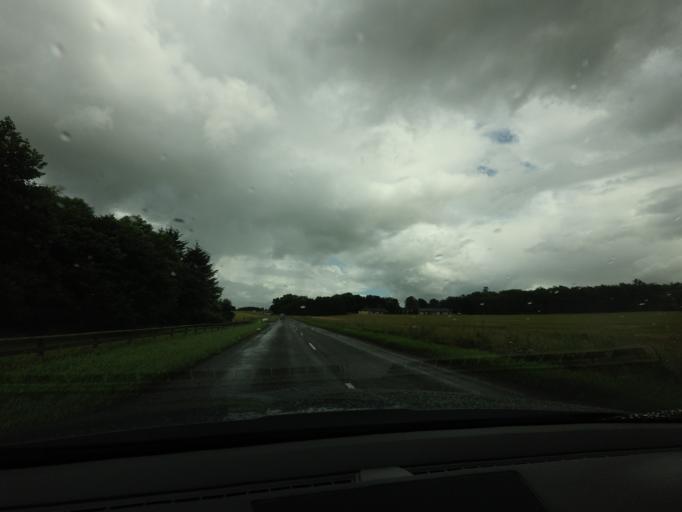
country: GB
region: Scotland
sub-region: Aberdeenshire
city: Turriff
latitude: 57.5554
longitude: -2.4390
